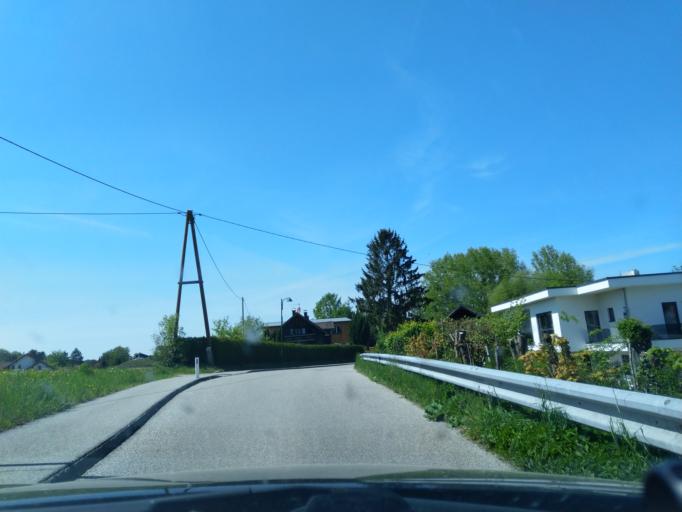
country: AT
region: Upper Austria
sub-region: Politischer Bezirk Ried im Innkreis
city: Ried im Innkreis
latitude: 48.2282
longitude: 13.4947
